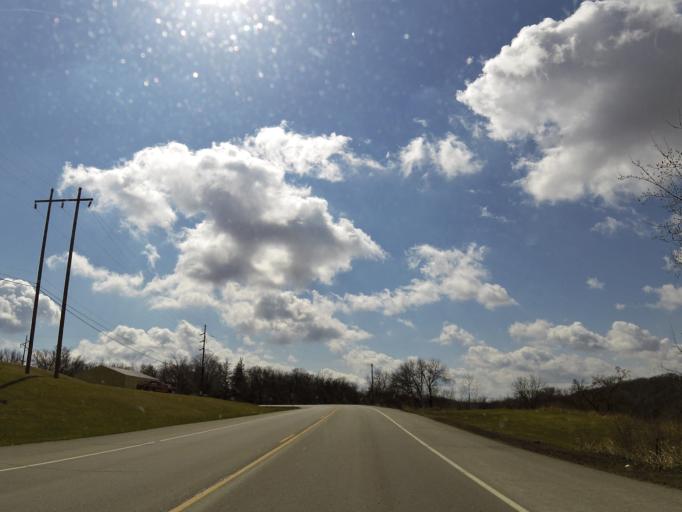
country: US
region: Minnesota
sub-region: Goodhue County
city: Kenyon
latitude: 44.2771
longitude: -92.9832
